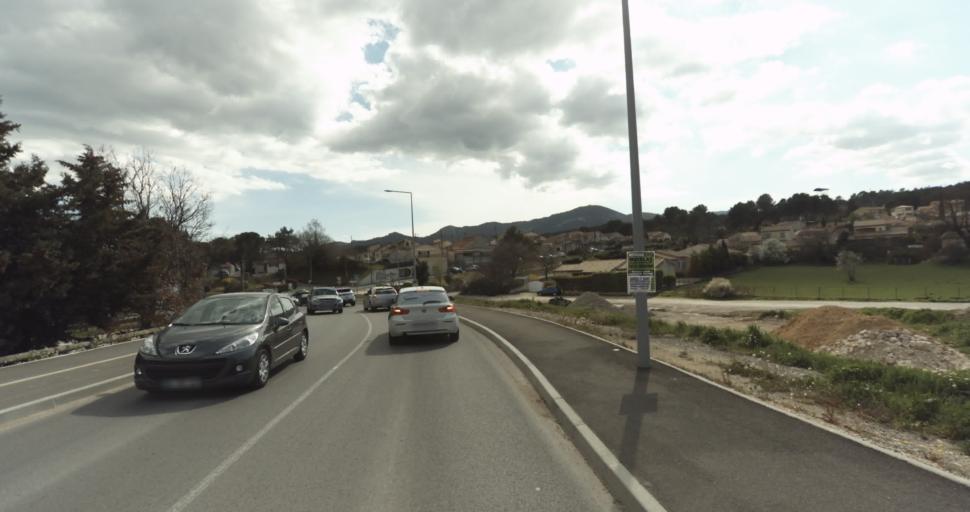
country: FR
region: Provence-Alpes-Cote d'Azur
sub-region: Departement des Bouches-du-Rhone
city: Greasque
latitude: 43.4354
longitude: 5.5384
